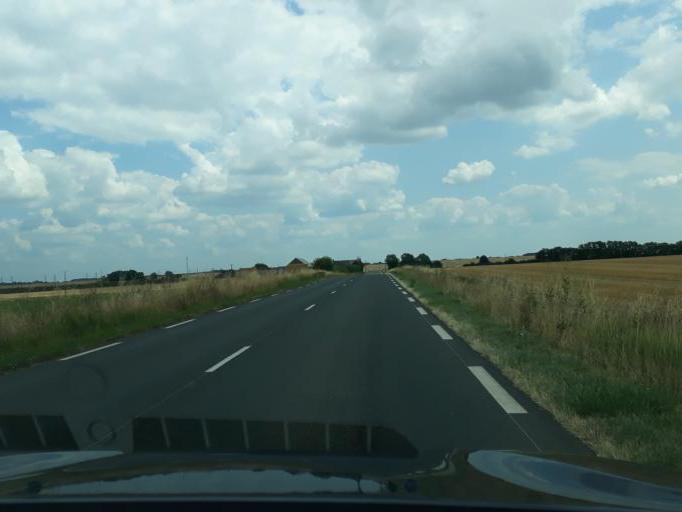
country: FR
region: Centre
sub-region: Departement du Cher
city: Avord
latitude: 47.0184
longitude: 2.7011
